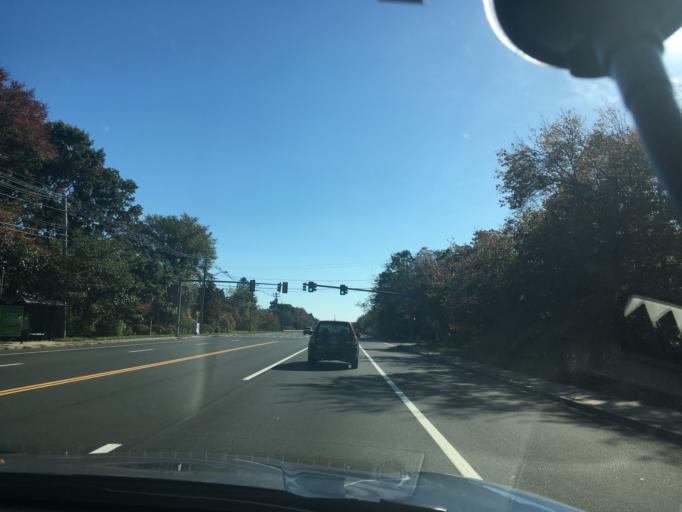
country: US
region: Rhode Island
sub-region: Washington County
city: Narragansett Pier
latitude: 41.4134
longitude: -71.4783
